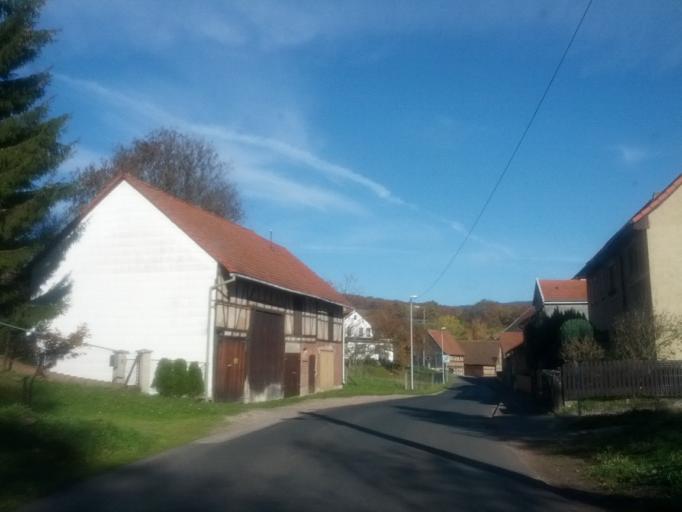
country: DE
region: Thuringia
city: Seebach
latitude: 50.9436
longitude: 10.4260
